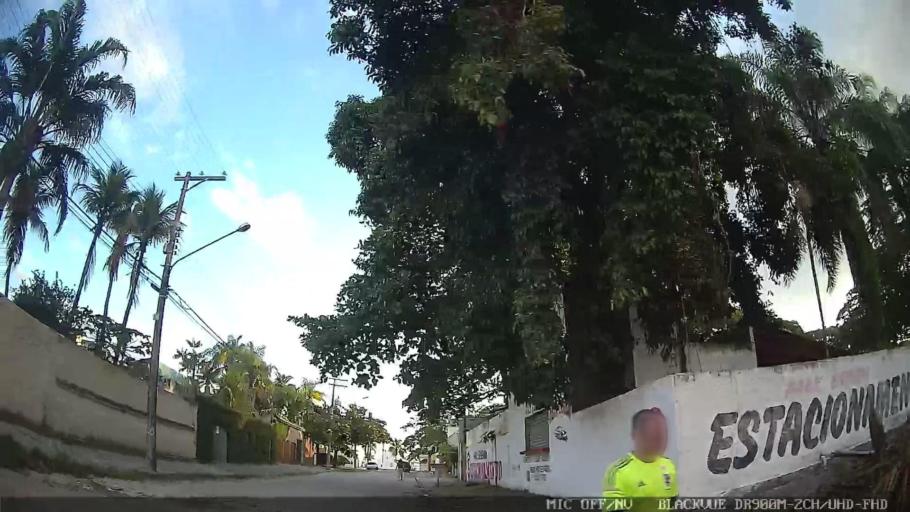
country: BR
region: Sao Paulo
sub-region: Guaruja
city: Guaruja
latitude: -23.9856
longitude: -46.2062
